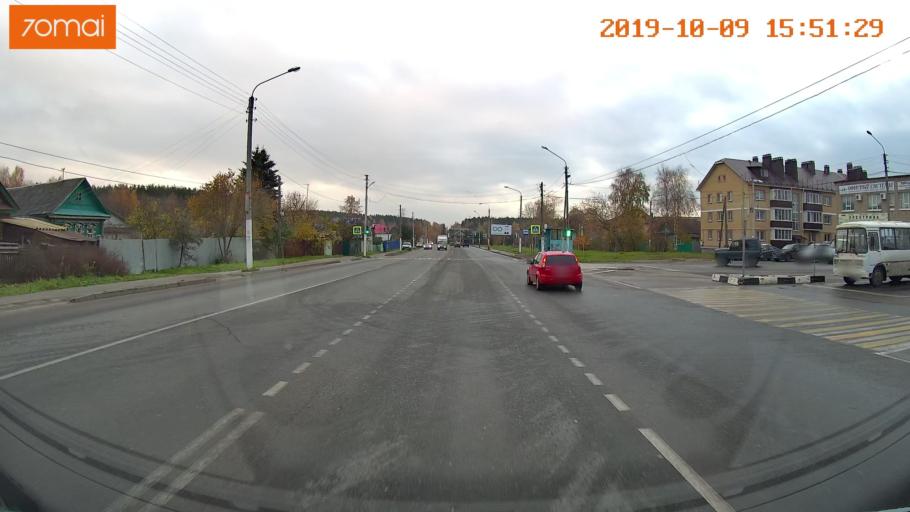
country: RU
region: Kostroma
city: Oktyabr'skiy
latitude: 57.7972
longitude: 40.9789
